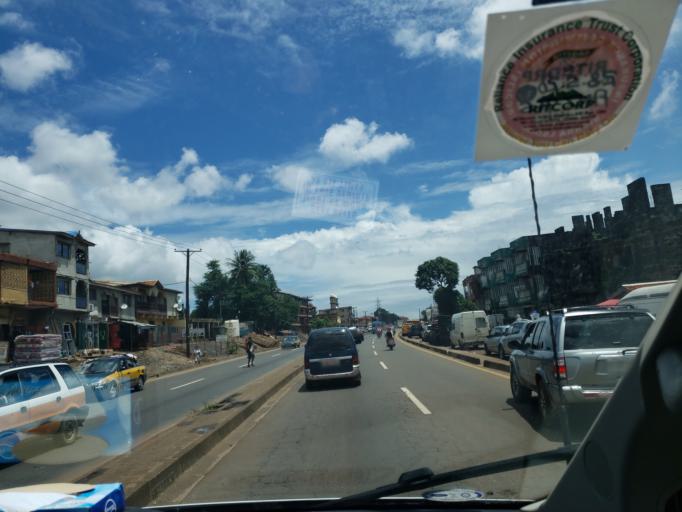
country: SL
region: Western Area
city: Freetown
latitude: 8.4553
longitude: -13.1709
